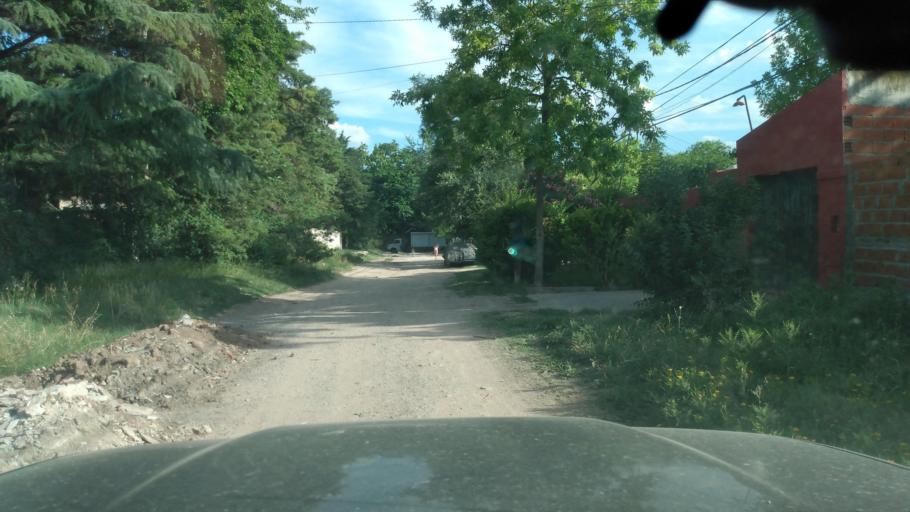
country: AR
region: Buenos Aires
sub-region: Partido de Lujan
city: Lujan
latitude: -34.5578
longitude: -59.1259
